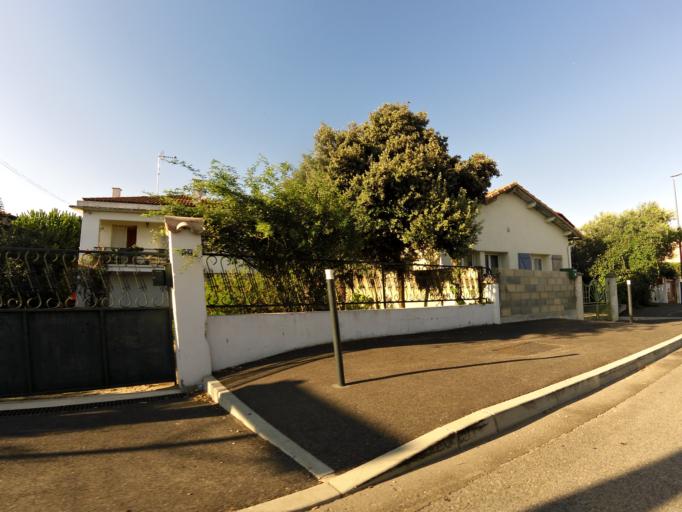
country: FR
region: Languedoc-Roussillon
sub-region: Departement du Gard
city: Remoulins
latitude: 43.9390
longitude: 4.5673
